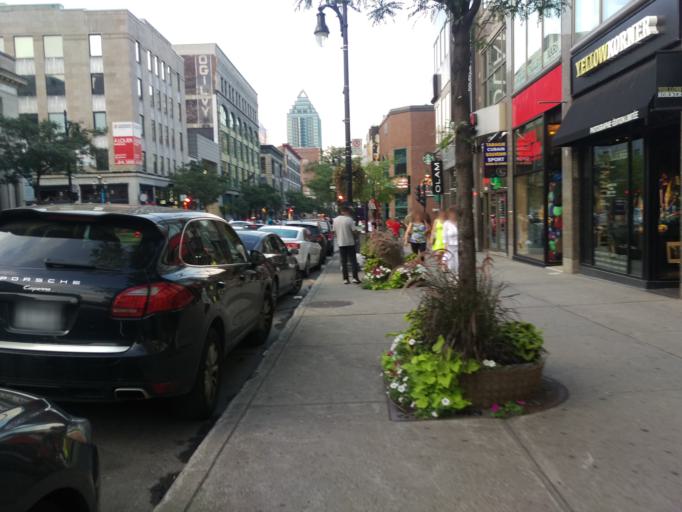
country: CA
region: Quebec
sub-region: Montreal
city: Montreal
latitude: 45.4969
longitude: -73.5760
